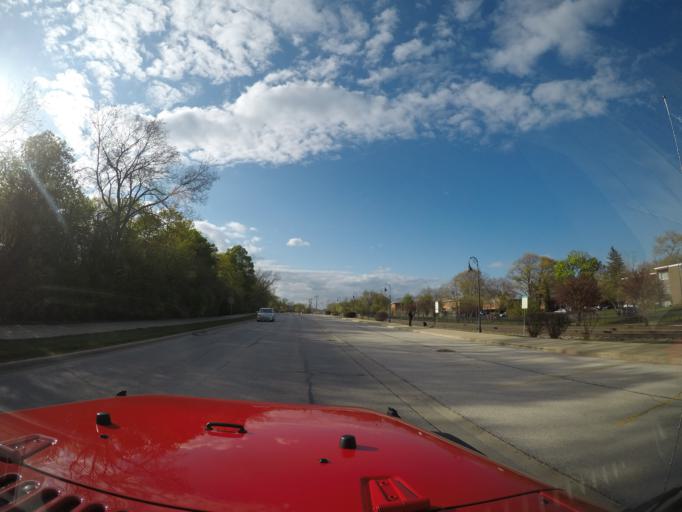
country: US
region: Illinois
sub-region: Cook County
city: Glenview
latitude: 42.0785
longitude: -87.8079
